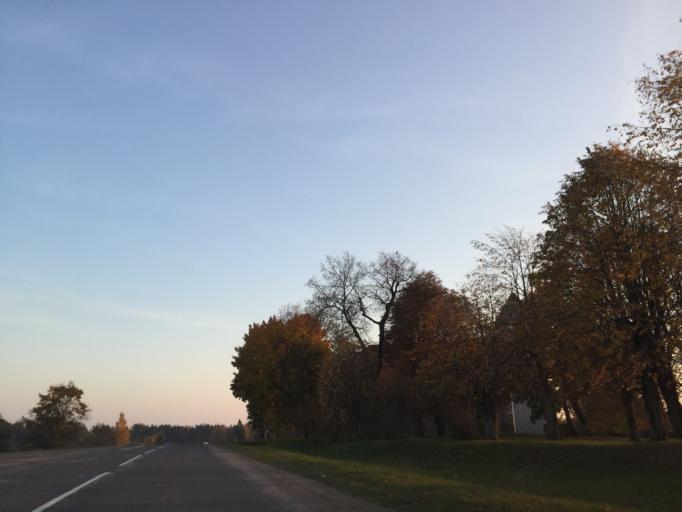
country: LV
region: Priekule
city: Priekule
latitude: 56.3664
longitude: 21.6030
